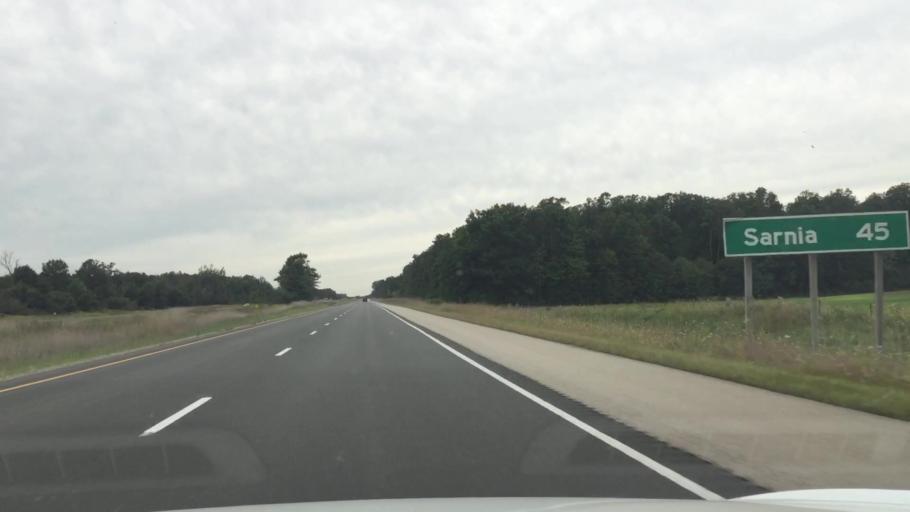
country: CA
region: Ontario
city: Lambton Shores
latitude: 42.9922
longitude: -81.8886
